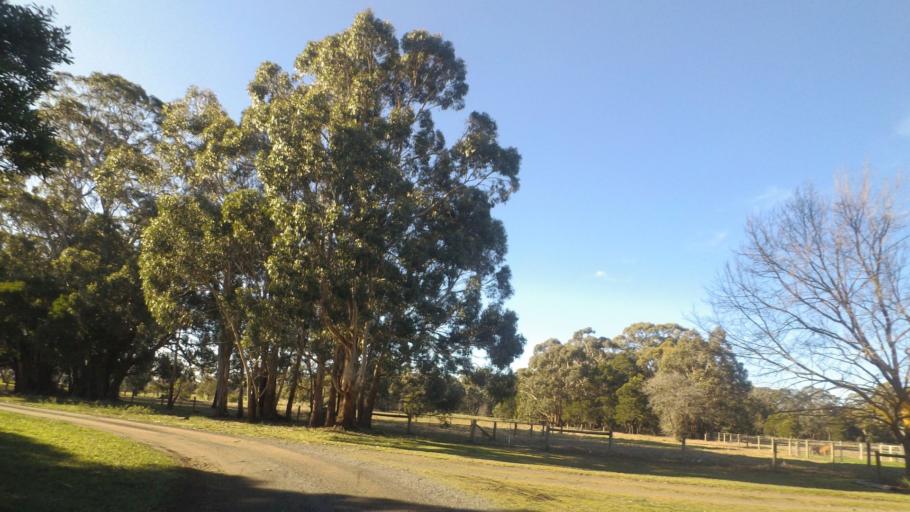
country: AU
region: Victoria
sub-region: Mount Alexander
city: Castlemaine
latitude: -37.3034
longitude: 144.3350
